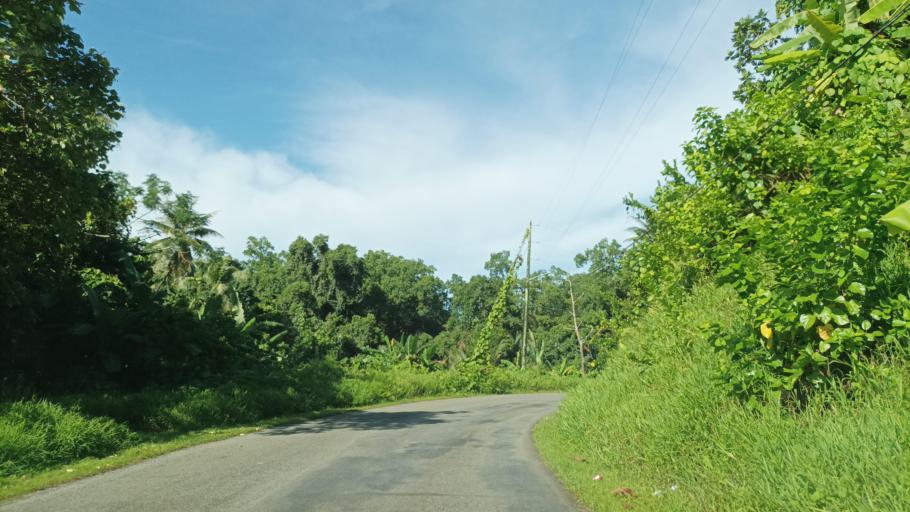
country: FM
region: Kosrae
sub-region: Lelu Municipality
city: Tofol
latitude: 5.3210
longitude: 163.0131
